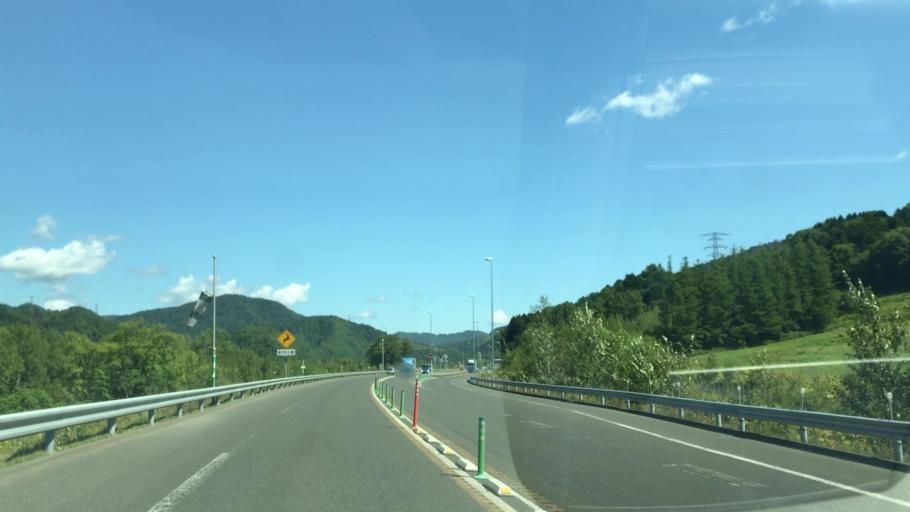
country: JP
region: Hokkaido
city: Shimo-furano
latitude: 43.0041
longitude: 142.4136
